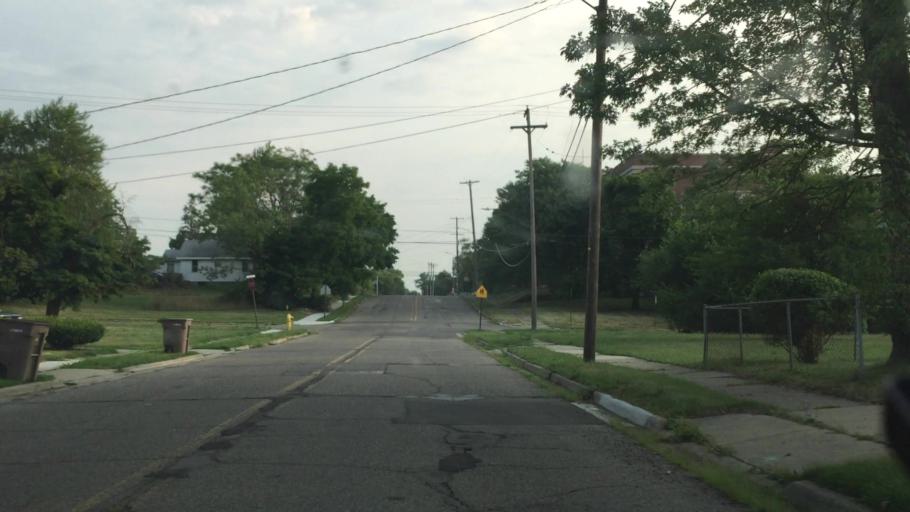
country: US
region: Michigan
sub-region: Oakland County
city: Pontiac
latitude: 42.6362
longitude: -83.2751
